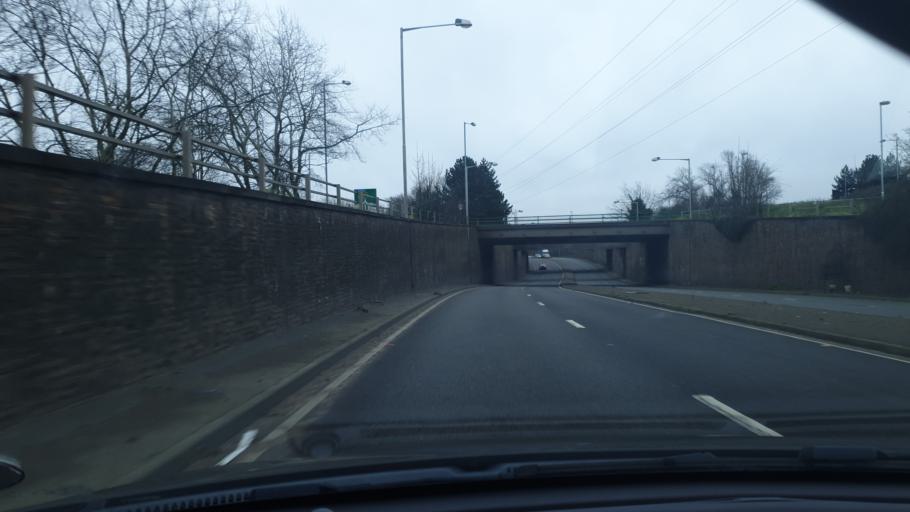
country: GB
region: England
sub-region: Walsall
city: Willenhall
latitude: 52.5780
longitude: -2.0569
